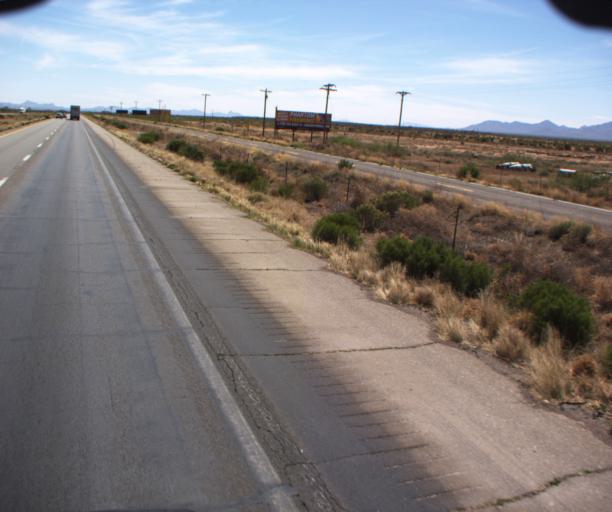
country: US
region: Arizona
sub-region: Cochise County
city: Willcox
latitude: 32.3163
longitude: -109.4379
